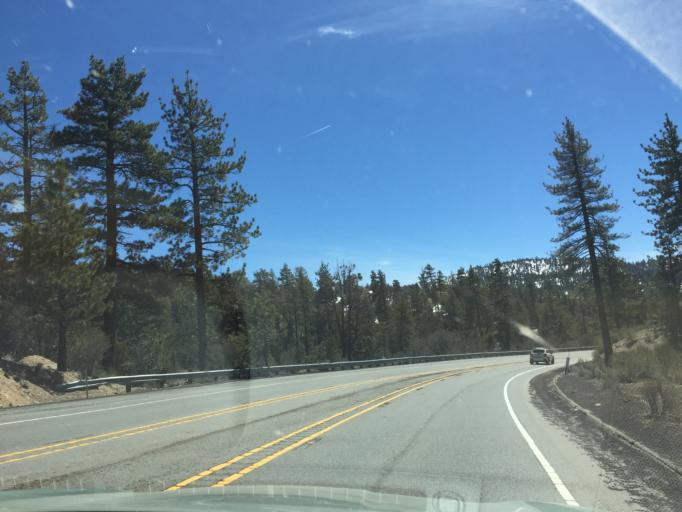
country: US
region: California
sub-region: San Bernardino County
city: Big Bear City
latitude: 34.1807
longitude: -116.7145
